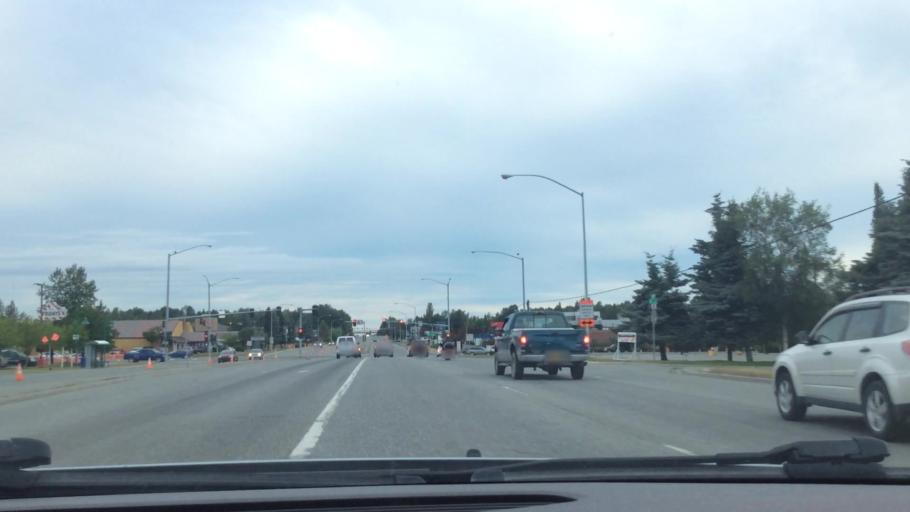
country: US
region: Alaska
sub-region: Anchorage Municipality
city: Anchorage
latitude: 61.1812
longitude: -149.8840
